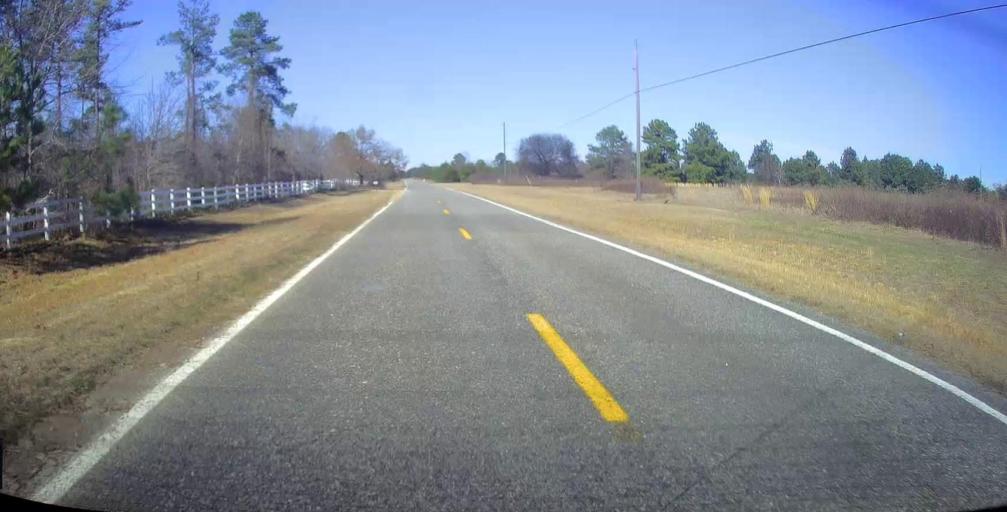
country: US
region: Georgia
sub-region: Peach County
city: Fort Valley
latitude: 32.6294
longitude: -83.9438
